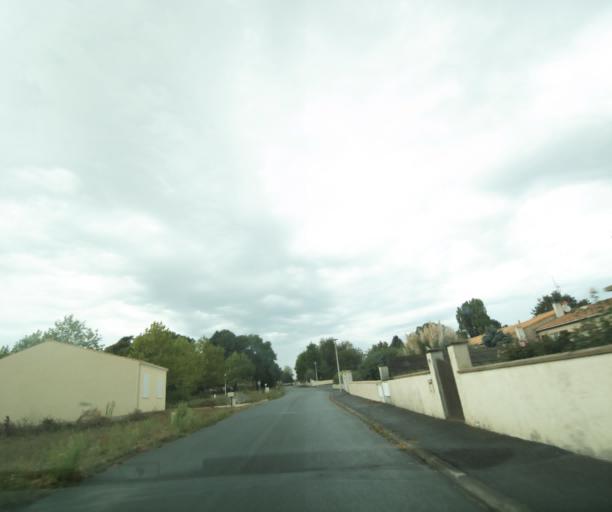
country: FR
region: Poitou-Charentes
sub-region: Departement de la Charente-Maritime
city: Tonnay-Charente
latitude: 45.9450
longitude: -0.8792
